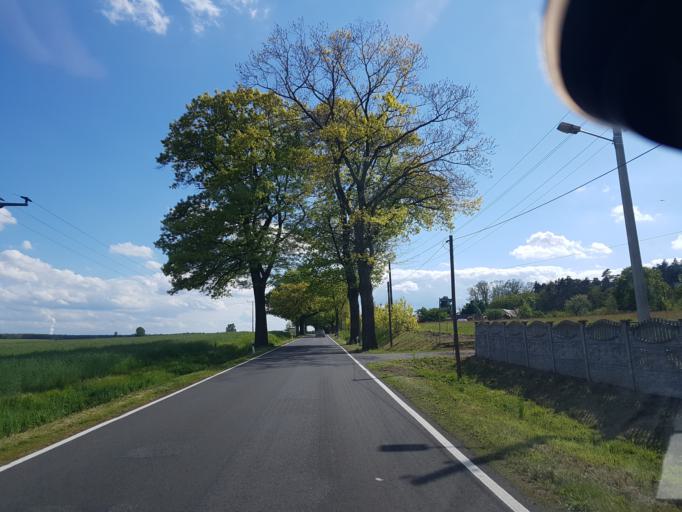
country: DE
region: Brandenburg
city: Cottbus
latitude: 51.6630
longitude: 14.3386
